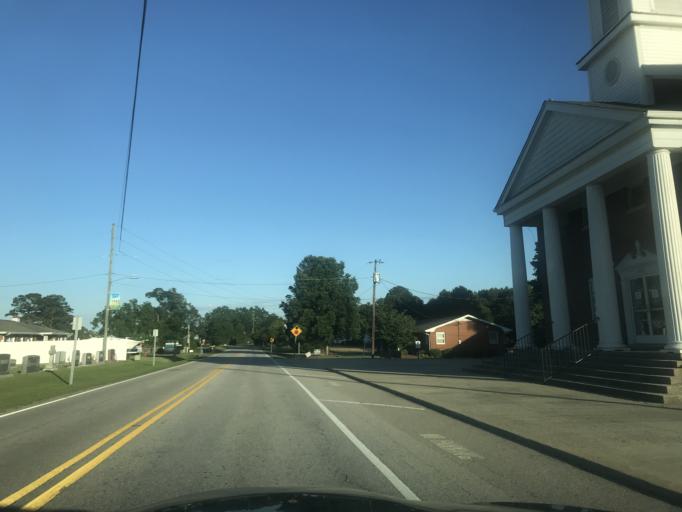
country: US
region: North Carolina
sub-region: Johnston County
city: Archer Lodge
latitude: 35.6940
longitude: -78.3753
